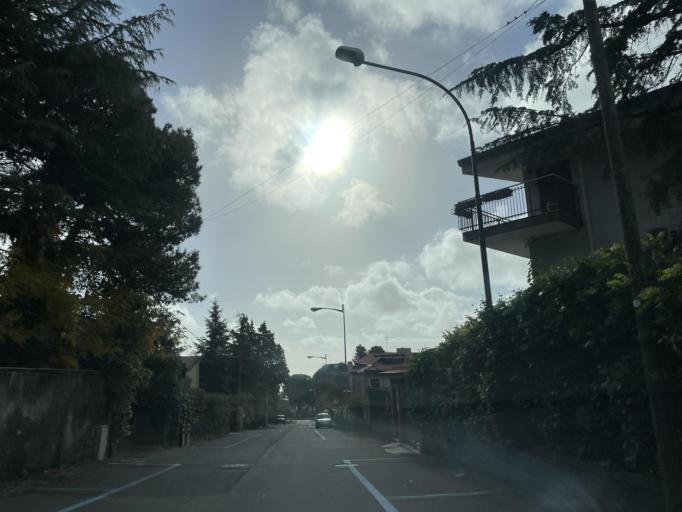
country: IT
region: Sicily
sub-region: Catania
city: Nicolosi
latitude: 37.6195
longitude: 15.0246
